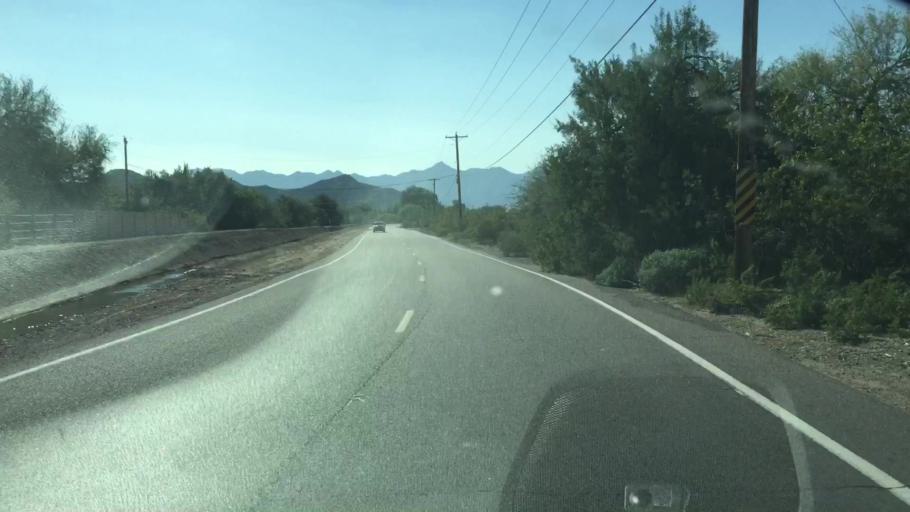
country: US
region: Arizona
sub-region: Maricopa County
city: Laveen
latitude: 33.3466
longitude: -112.1380
